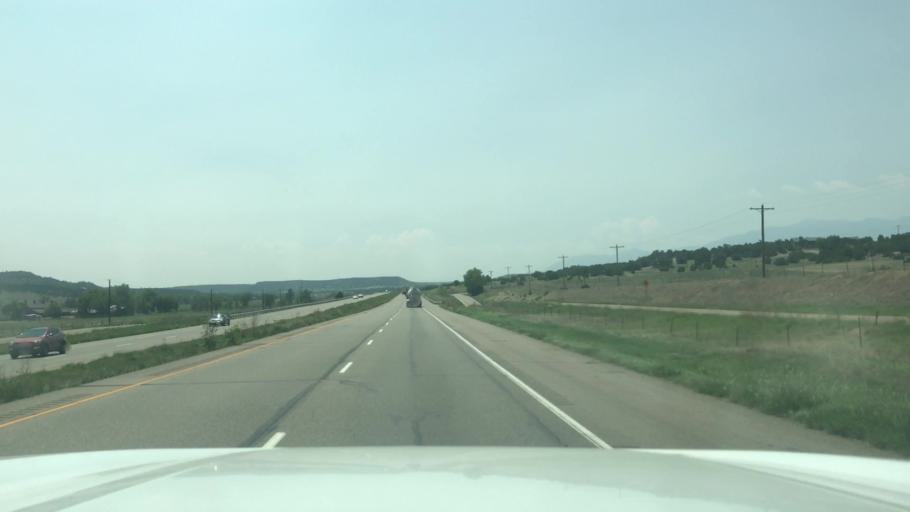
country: US
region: Colorado
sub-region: Pueblo County
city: Colorado City
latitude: 38.0120
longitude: -104.7462
